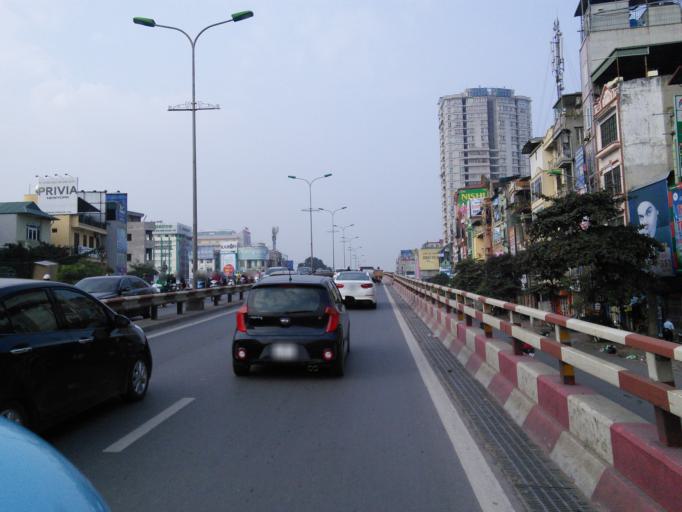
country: VN
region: Ha Noi
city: Hai BaTrung
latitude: 20.9963
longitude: 105.8413
